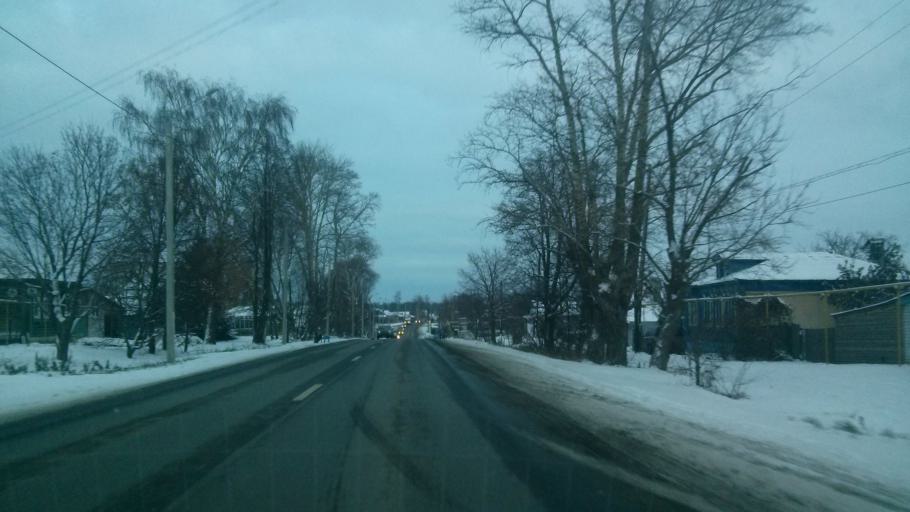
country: RU
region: Nizjnij Novgorod
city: Vorsma
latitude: 56.0348
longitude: 43.3667
